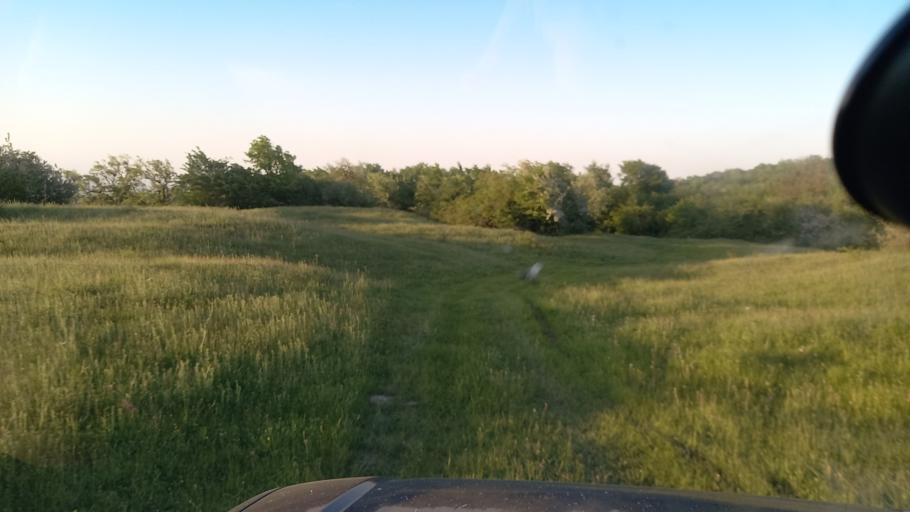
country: RU
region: Dagestan
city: Khuchni
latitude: 42.0078
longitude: 47.9730
